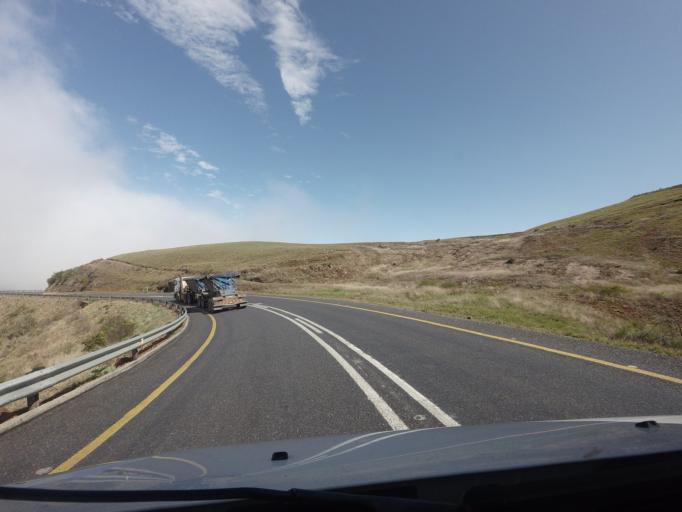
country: ZA
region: Mpumalanga
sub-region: Ehlanzeni District
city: Lydenburg
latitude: -25.1581
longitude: 30.6284
